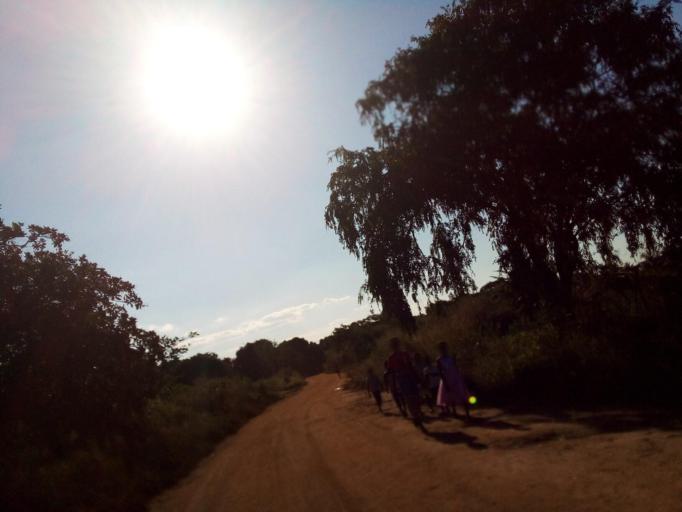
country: MZ
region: Zambezia
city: Quelimane
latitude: -17.4870
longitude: 36.5530
